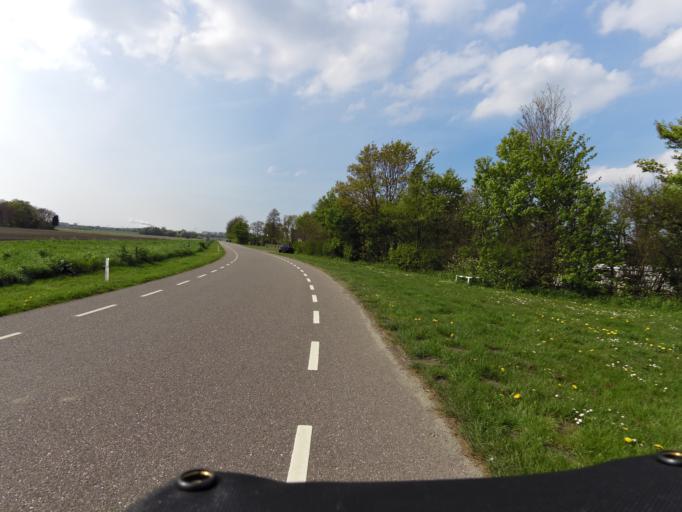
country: NL
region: South Holland
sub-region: Gemeente Brielle
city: Brielle
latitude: 51.9169
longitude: 4.1466
